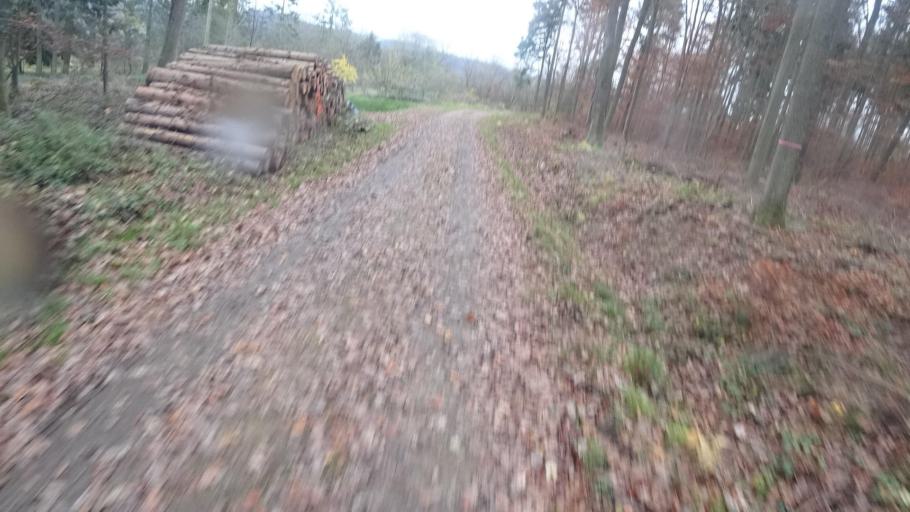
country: DE
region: Rheinland-Pfalz
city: Prath
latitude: 50.1637
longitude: 7.6752
